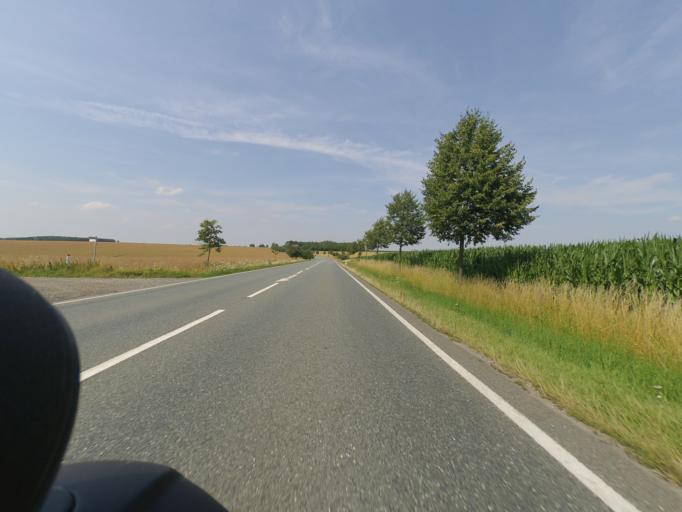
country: DE
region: Thuringia
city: Hirschfeld
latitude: 50.9708
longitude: 12.1352
